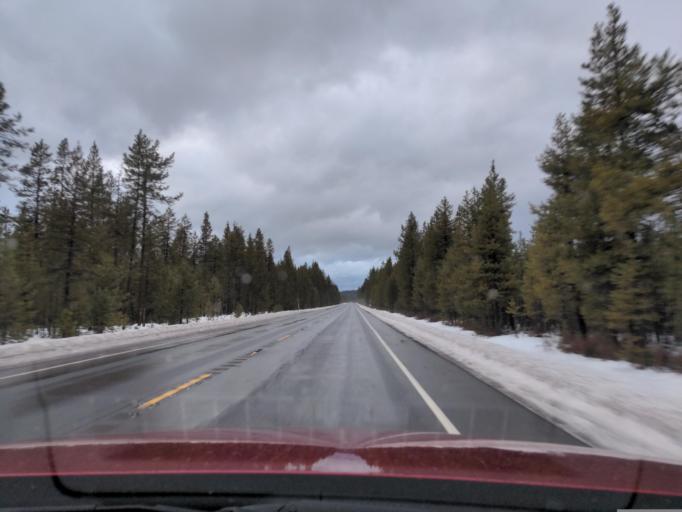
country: US
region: Oregon
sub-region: Deschutes County
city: La Pine
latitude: 43.4083
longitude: -121.8288
